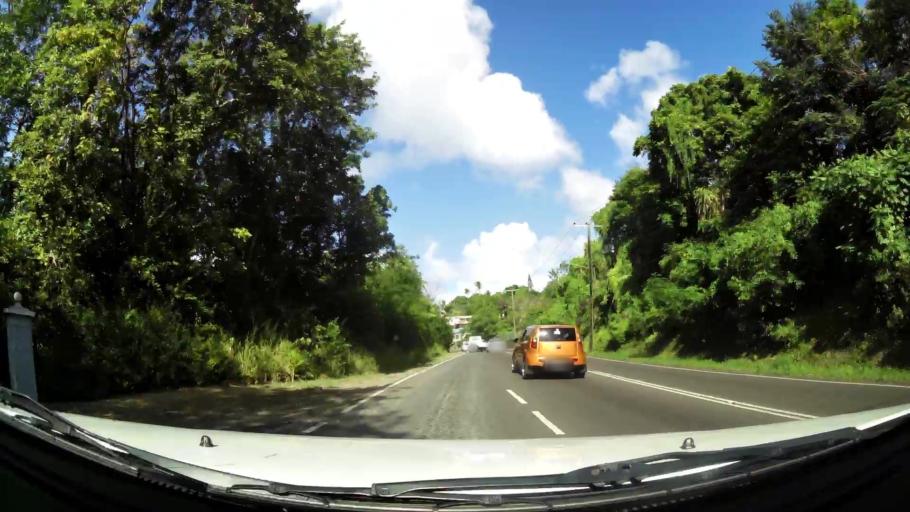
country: LC
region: Castries Quarter
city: Bisee
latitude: 14.0417
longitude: -60.9695
